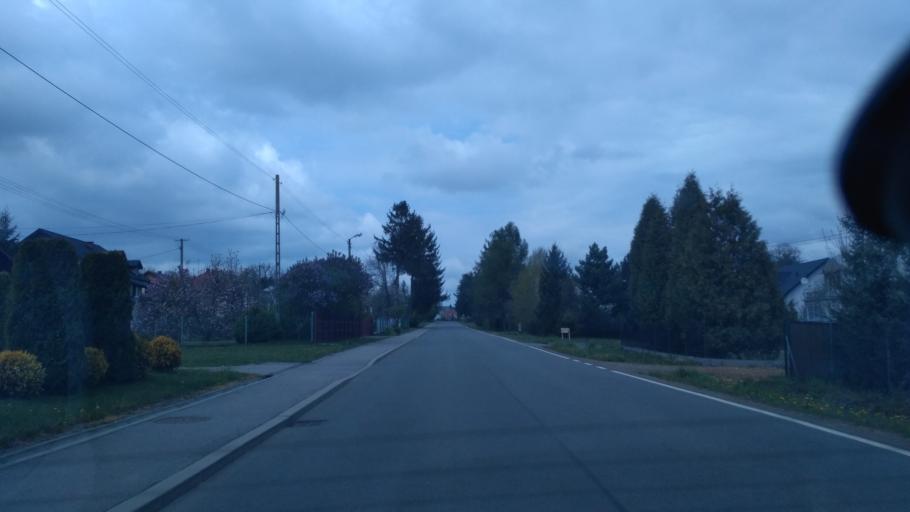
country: PL
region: Subcarpathian Voivodeship
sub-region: Powiat brzozowski
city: Jasionow
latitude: 49.6477
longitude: 21.9771
